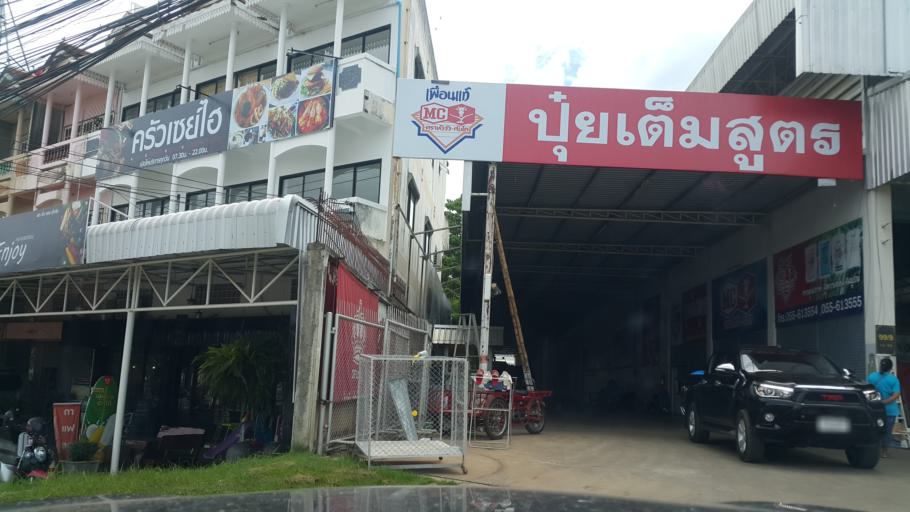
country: TH
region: Sukhothai
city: Sukhothai
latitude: 17.0164
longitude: 99.8101
